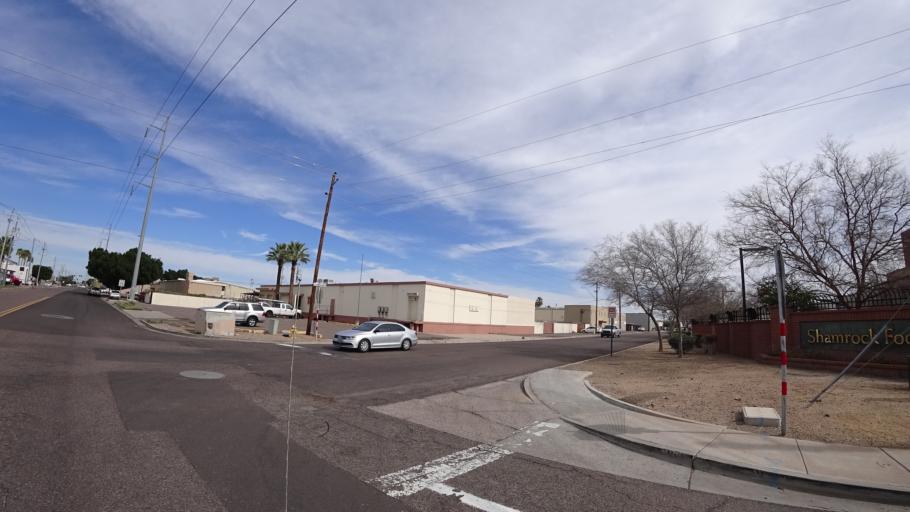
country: US
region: Arizona
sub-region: Maricopa County
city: Phoenix
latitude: 33.4767
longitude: -112.1257
